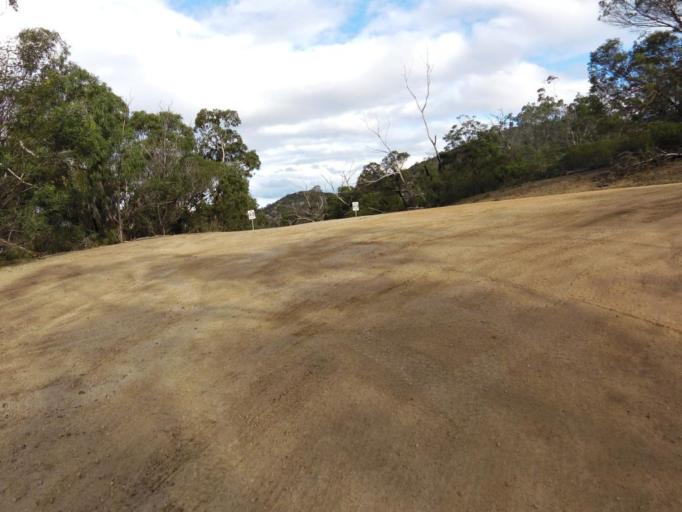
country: AU
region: Victoria
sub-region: Wyndham
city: Little River
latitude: -37.9371
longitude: 144.4395
